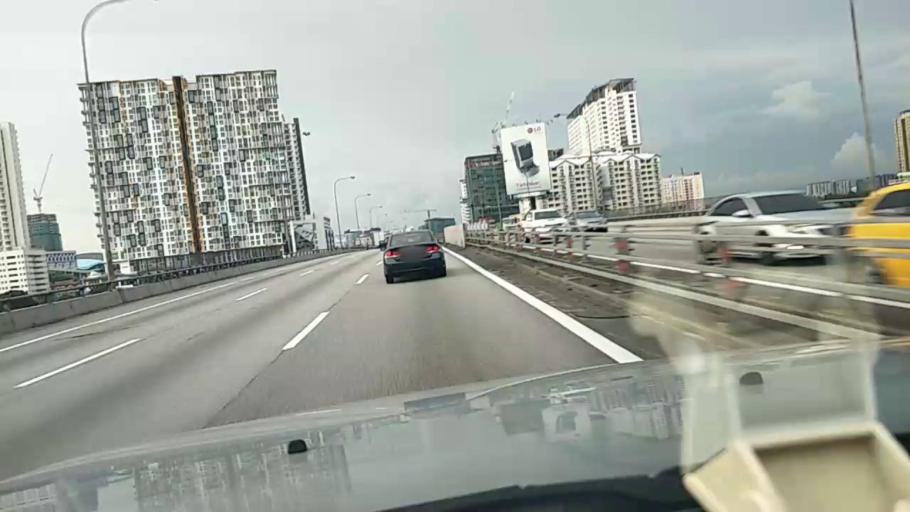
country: MY
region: Selangor
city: Shah Alam
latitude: 3.0716
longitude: 101.5536
